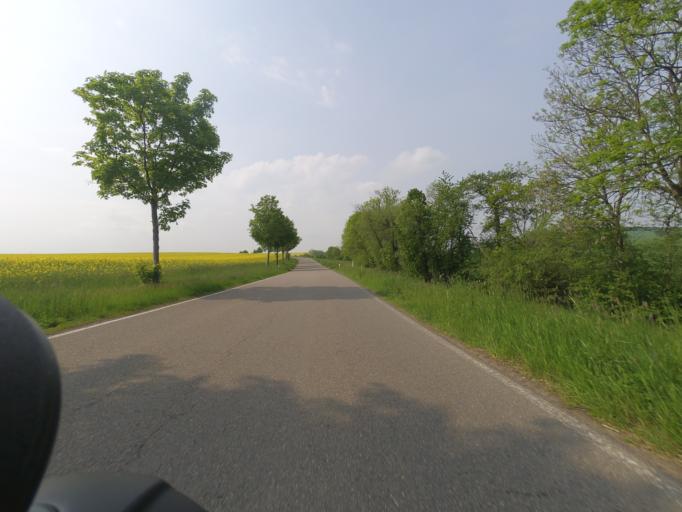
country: DE
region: Saxony
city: Obercunnersdorf
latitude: 50.9007
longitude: 13.5950
